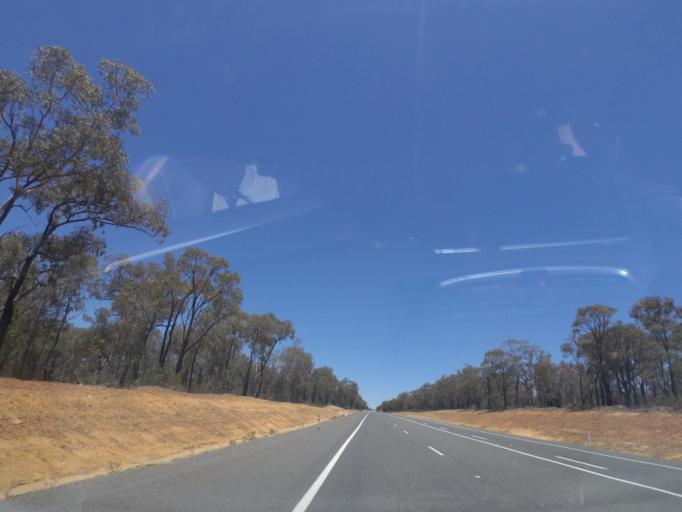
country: AU
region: New South Wales
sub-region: Warrumbungle Shire
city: Coonabarabran
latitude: -30.8948
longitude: 149.4412
